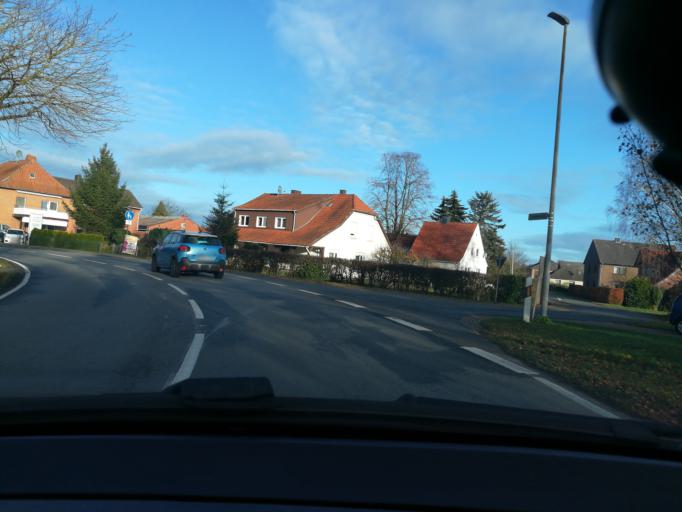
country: DE
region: Lower Saxony
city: Schwaforden
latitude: 52.7343
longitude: 8.8174
